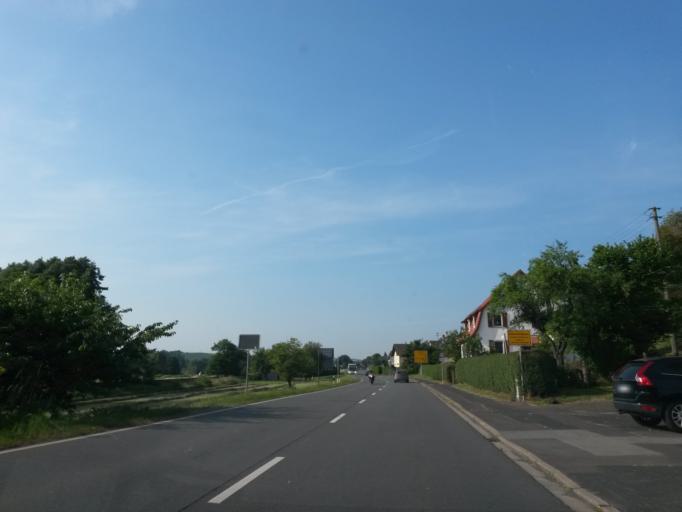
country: DE
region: Hesse
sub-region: Regierungsbezirk Giessen
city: Munchhausen
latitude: 50.9300
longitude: 8.7049
